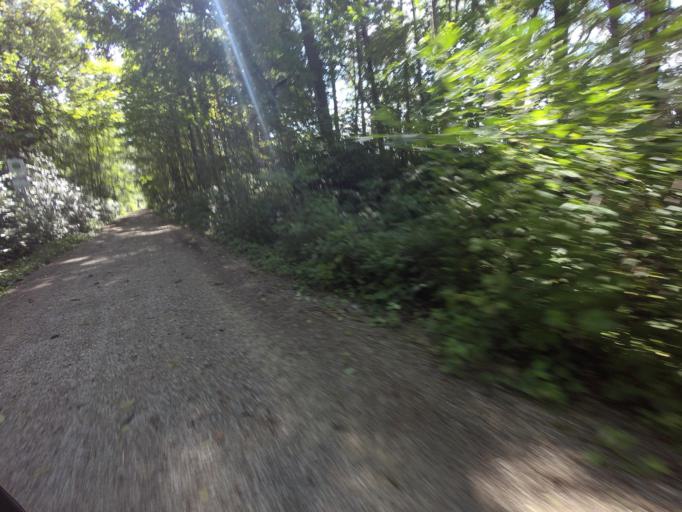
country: CA
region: Ontario
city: Huron East
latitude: 43.6923
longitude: -81.3288
